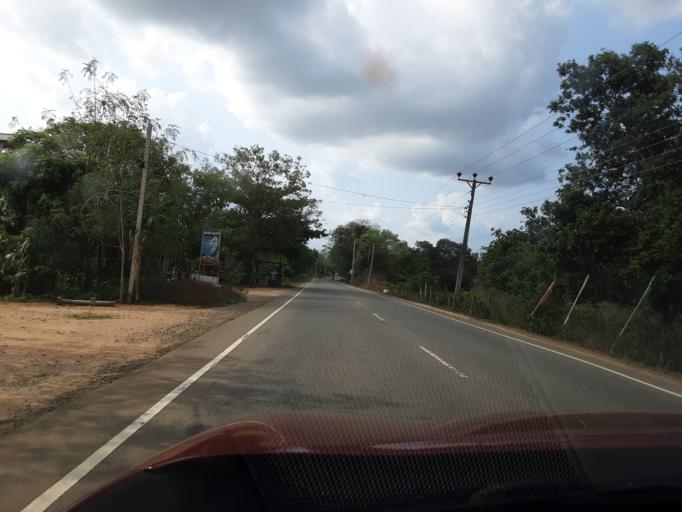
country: LK
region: Uva
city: Haputale
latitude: 6.5136
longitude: 81.1285
